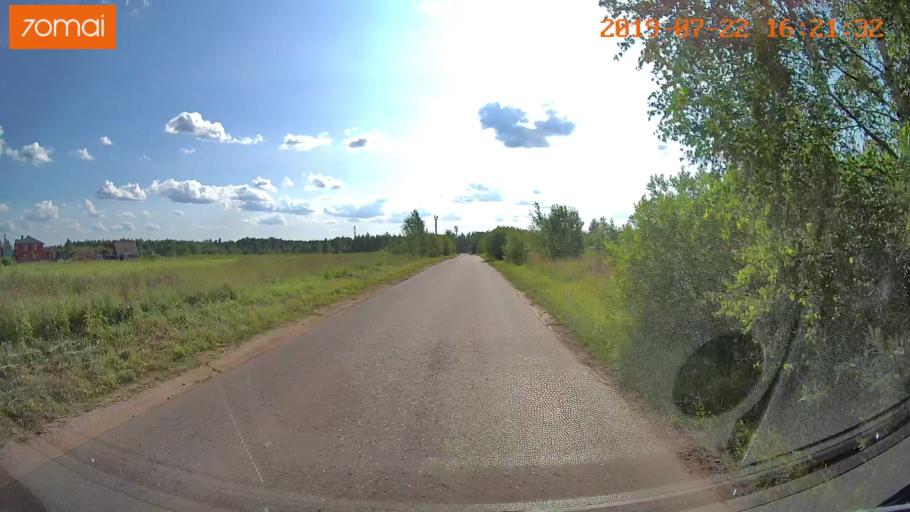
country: RU
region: Ivanovo
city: Novo-Talitsy
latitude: 57.0617
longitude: 40.8850
